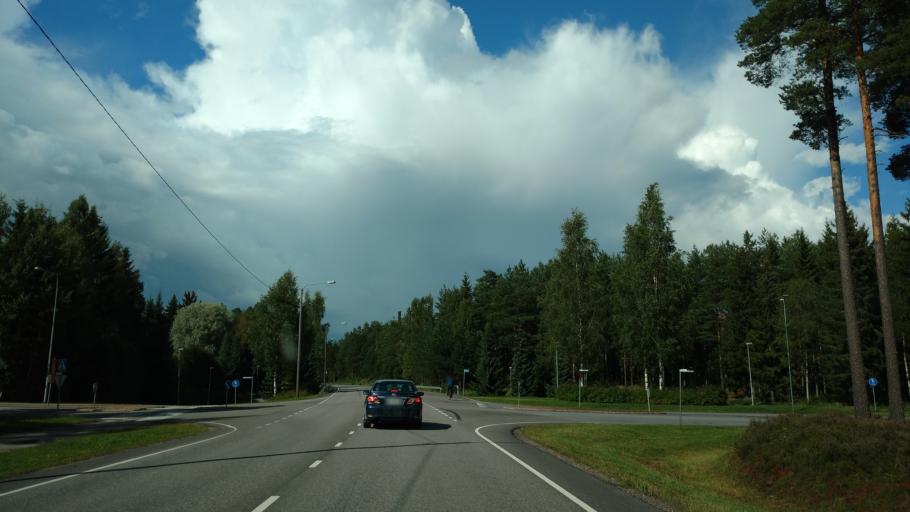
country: FI
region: Varsinais-Suomi
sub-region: Turku
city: Paimio
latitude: 60.4456
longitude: 22.7082
